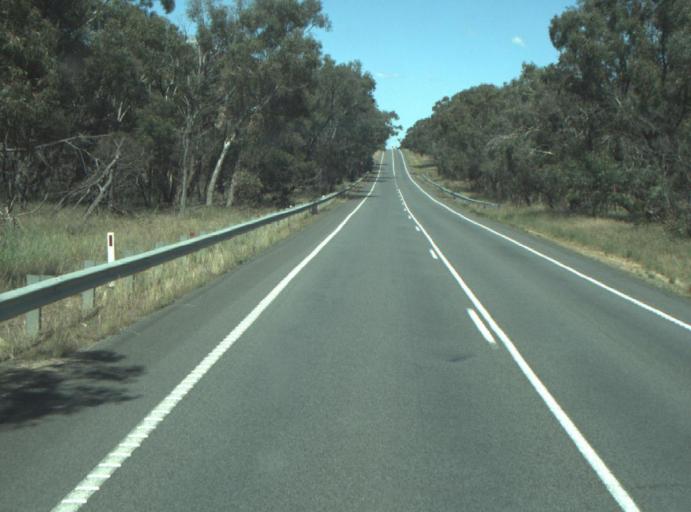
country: AU
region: Victoria
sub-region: Greater Geelong
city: Lara
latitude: -37.9150
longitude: 144.3668
